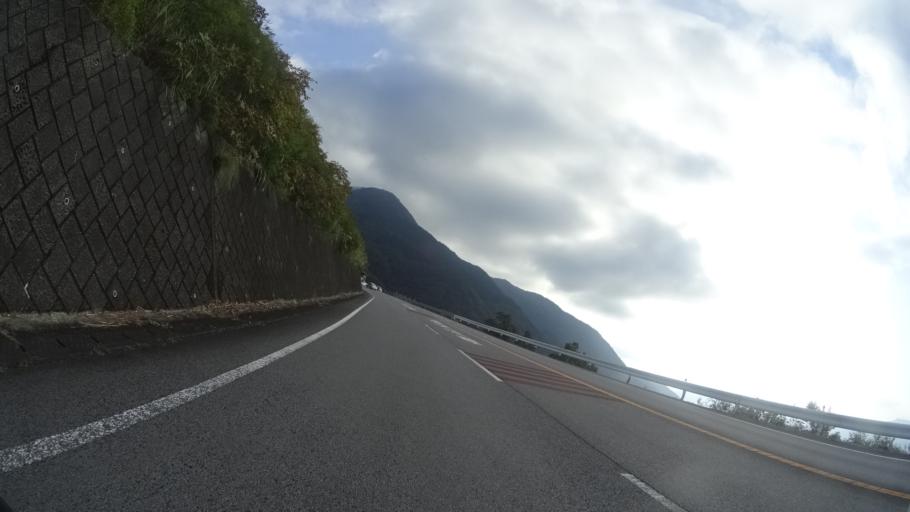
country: JP
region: Oita
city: Beppu
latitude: 33.2614
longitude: 131.3829
